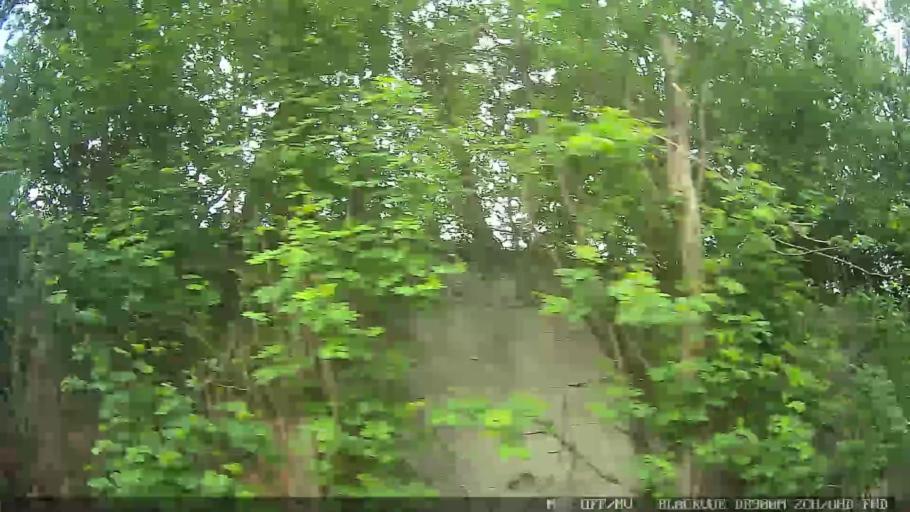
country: BR
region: Sao Paulo
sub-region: Jaguariuna
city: Jaguariuna
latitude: -22.6816
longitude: -47.0169
